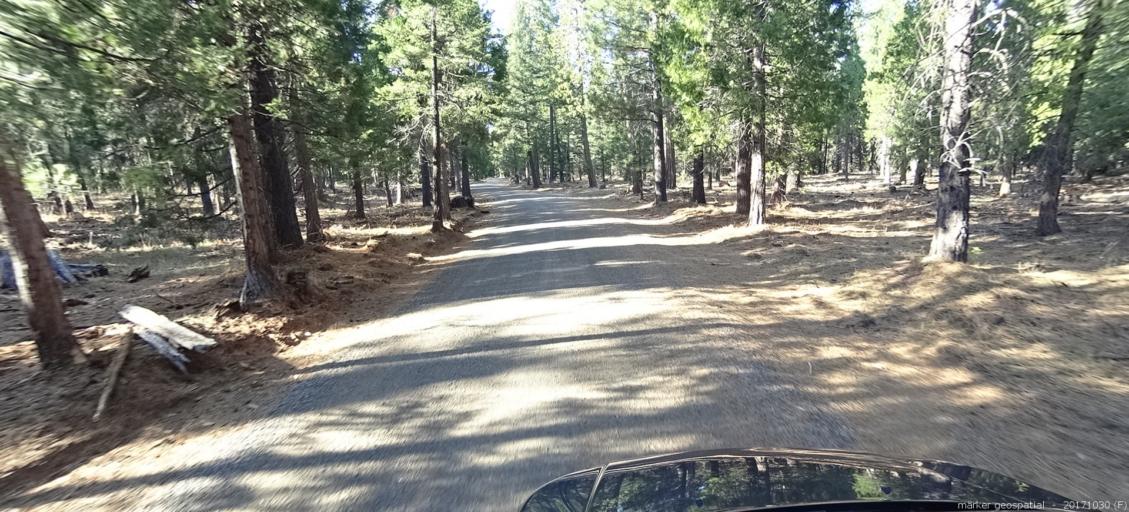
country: US
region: California
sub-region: Shasta County
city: Shingletown
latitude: 40.5592
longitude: -121.7369
